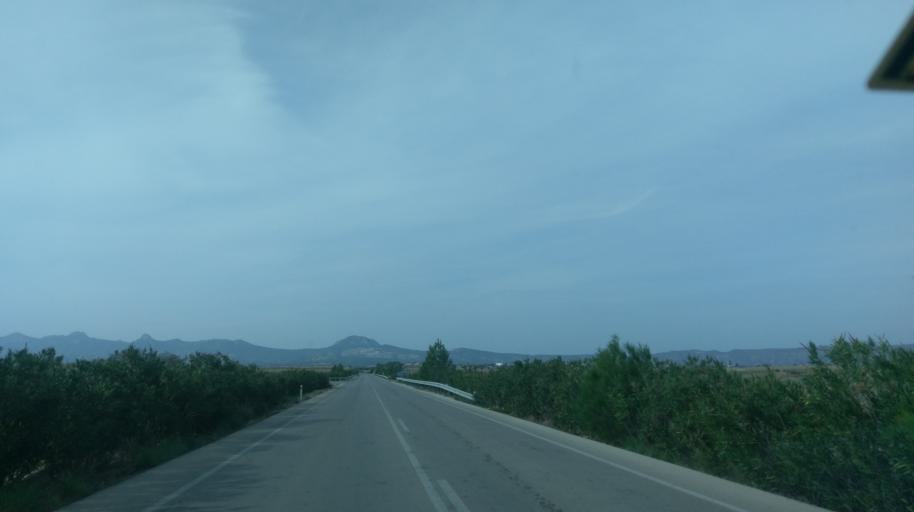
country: CY
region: Ammochostos
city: Leonarisso
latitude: 35.3795
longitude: 34.0228
